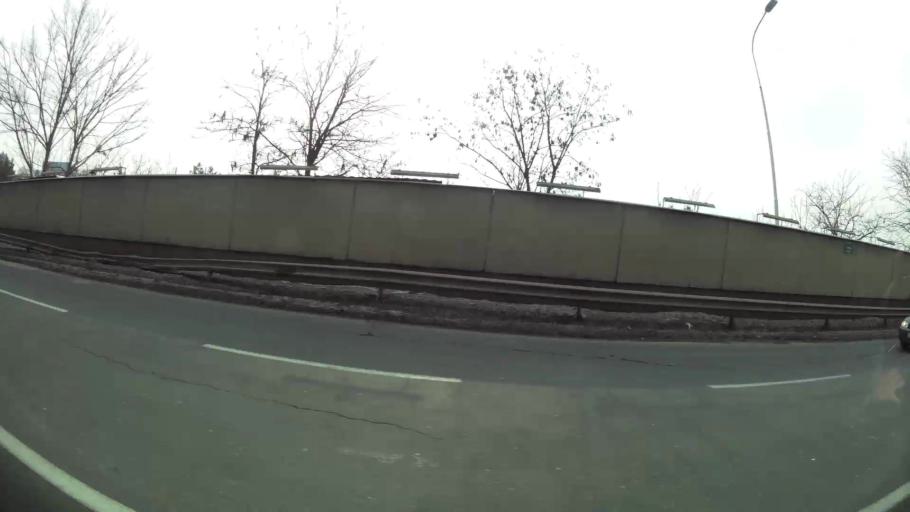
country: MK
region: Cair
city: Cair
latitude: 42.0125
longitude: 21.4235
